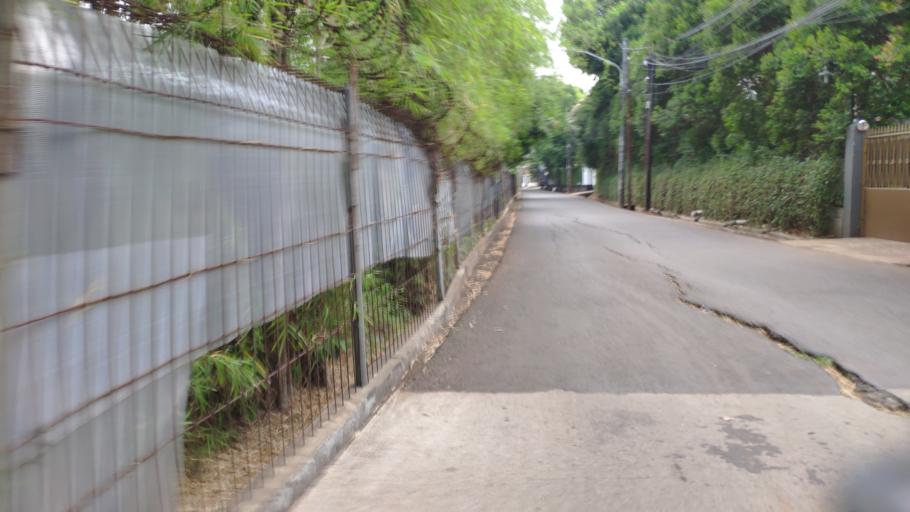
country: ID
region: Jakarta Raya
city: Jakarta
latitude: -6.2937
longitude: 106.8121
